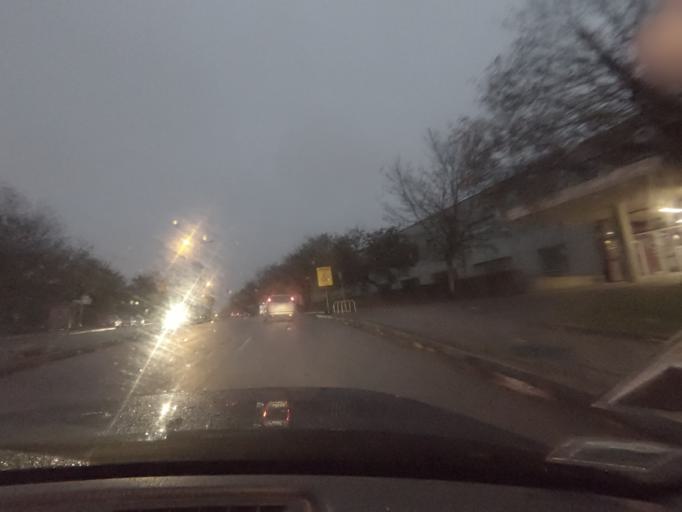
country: PT
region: Porto
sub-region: Matosinhos
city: Senhora da Hora
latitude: 41.1851
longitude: -8.6621
